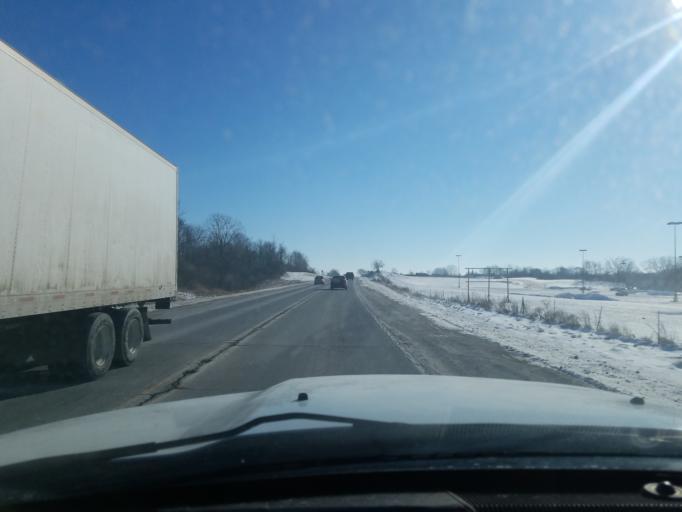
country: US
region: Indiana
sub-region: Noble County
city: Kendallville
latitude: 41.4506
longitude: -85.2438
